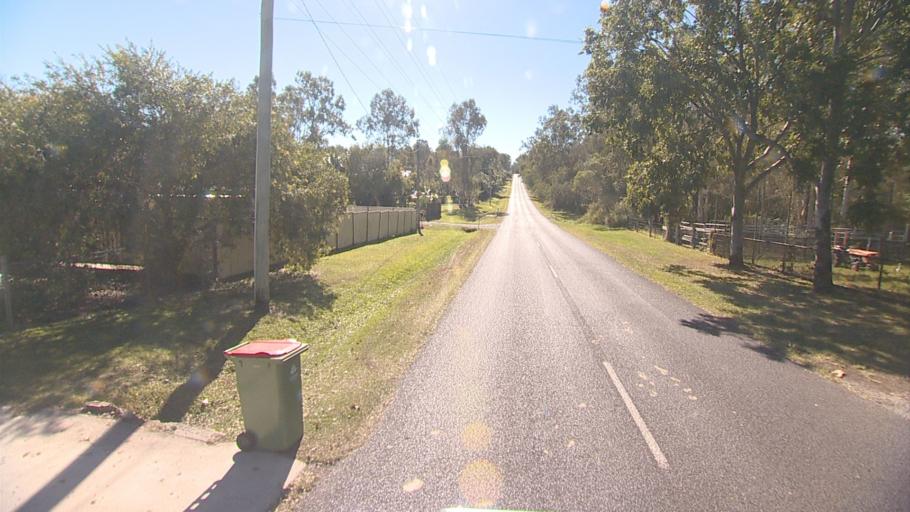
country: AU
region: Queensland
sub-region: Logan
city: Park Ridge South
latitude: -27.7175
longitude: 153.0576
